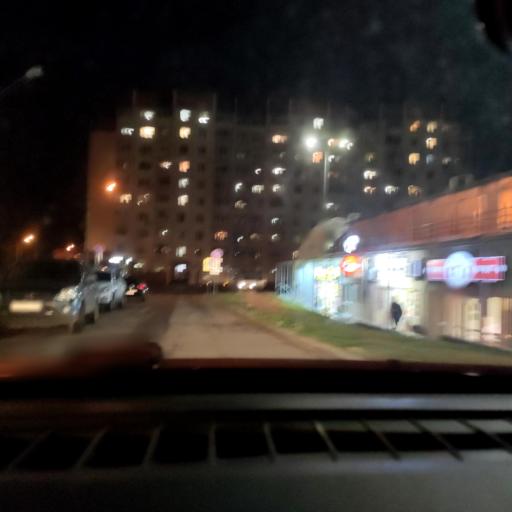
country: RU
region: Voronezj
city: Pridonskoy
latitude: 51.6247
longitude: 39.0769
